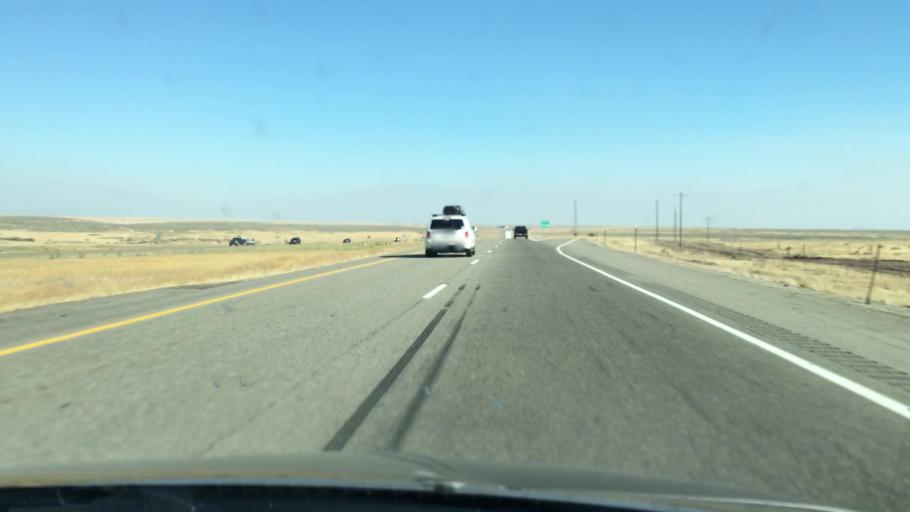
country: US
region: Idaho
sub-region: Ada County
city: Boise
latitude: 43.4677
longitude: -116.0971
